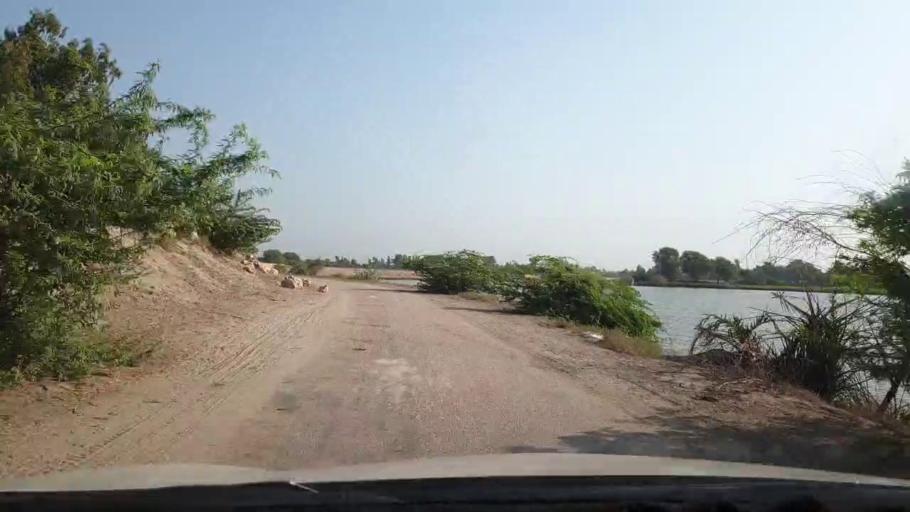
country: PK
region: Sindh
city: Larkana
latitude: 27.5494
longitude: 68.2561
